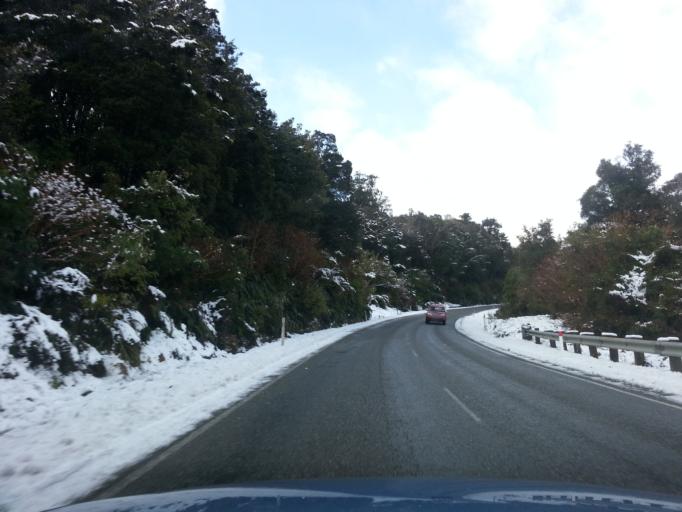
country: NZ
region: West Coast
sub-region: Grey District
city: Greymouth
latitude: -42.7960
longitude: 171.5832
